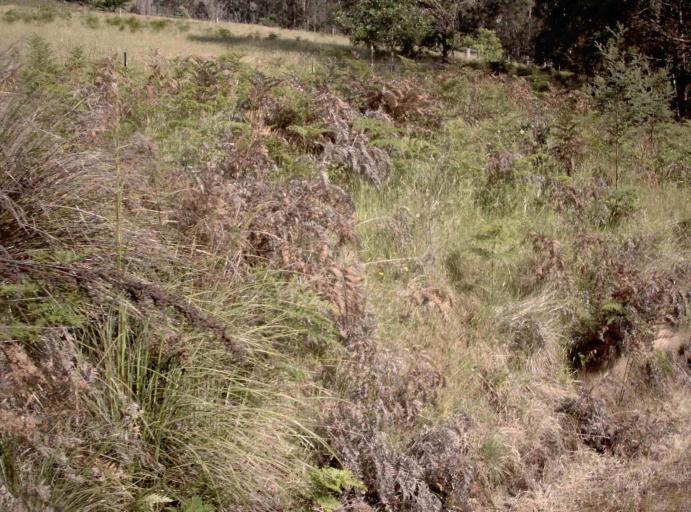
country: AU
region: Victoria
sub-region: East Gippsland
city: Lakes Entrance
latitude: -37.3977
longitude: 148.5928
